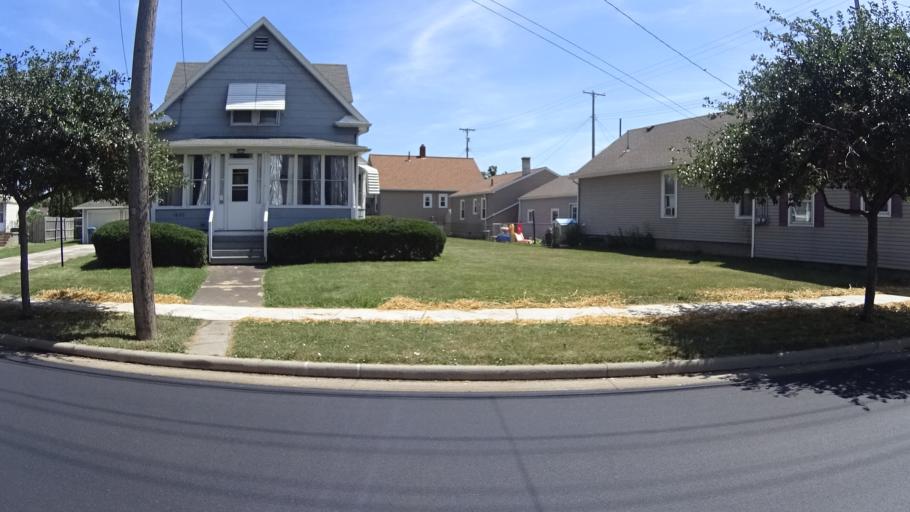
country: US
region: Ohio
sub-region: Erie County
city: Sandusky
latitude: 41.4402
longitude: -82.7059
